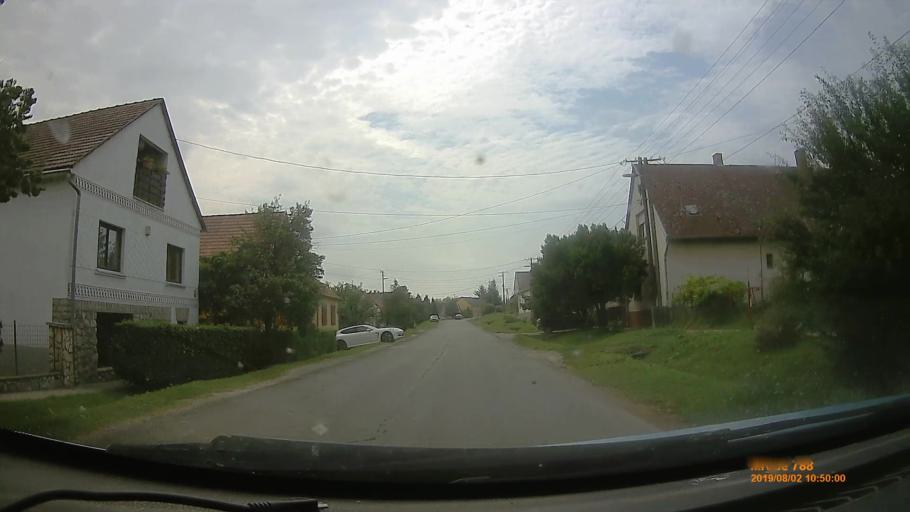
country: HU
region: Baranya
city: Buekkoesd
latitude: 46.0886
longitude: 17.9760
